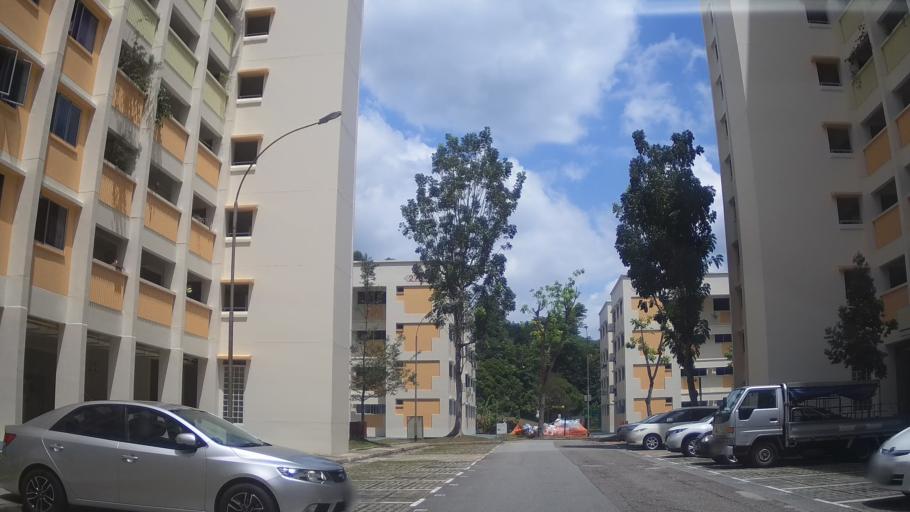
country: MY
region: Johor
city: Johor Bahru
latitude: 1.3770
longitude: 103.7750
